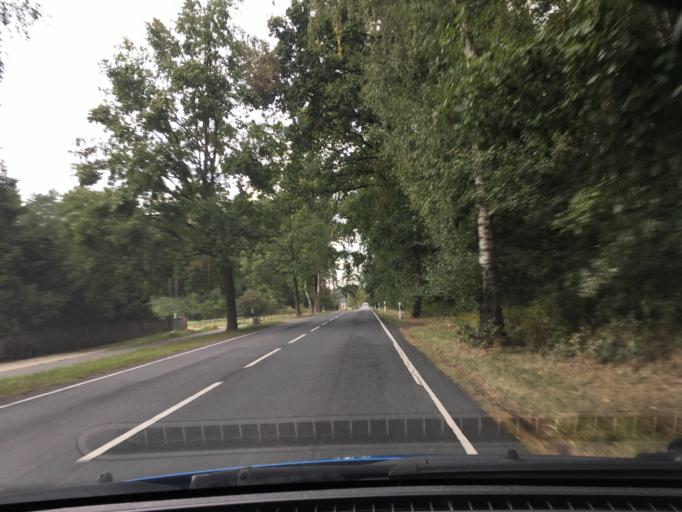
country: DE
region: Lower Saxony
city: Garstedt
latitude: 53.2754
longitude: 10.1654
